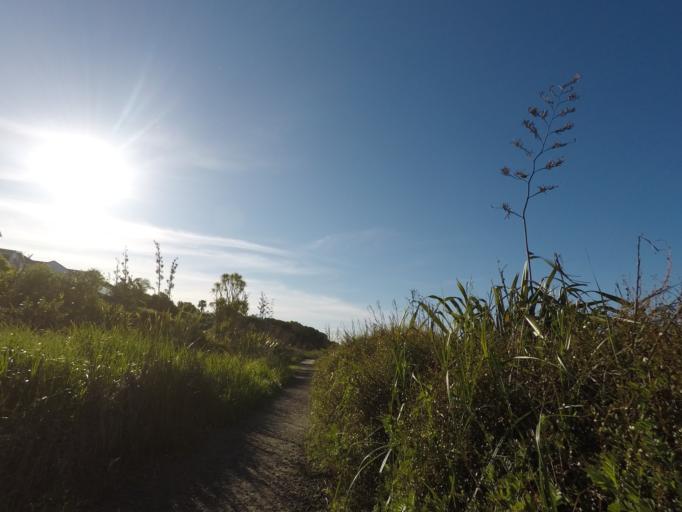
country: NZ
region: Auckland
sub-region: Auckland
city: Rosebank
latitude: -36.8309
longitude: 174.6599
